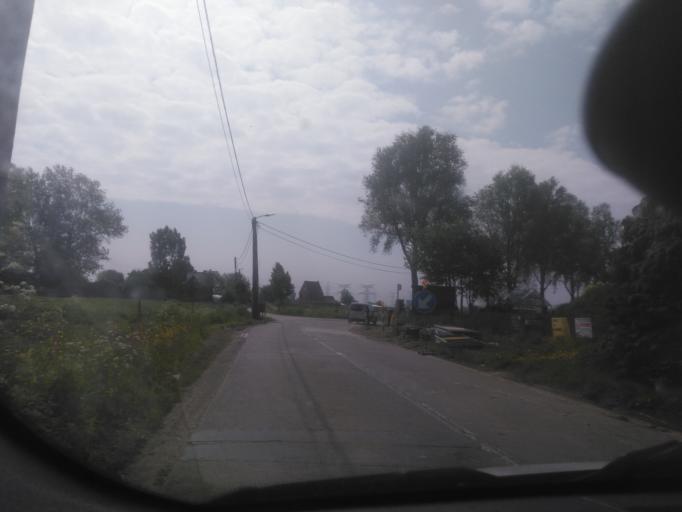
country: BE
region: Flanders
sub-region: Provincie Oost-Vlaanderen
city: Beveren
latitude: 51.2118
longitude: 4.2088
